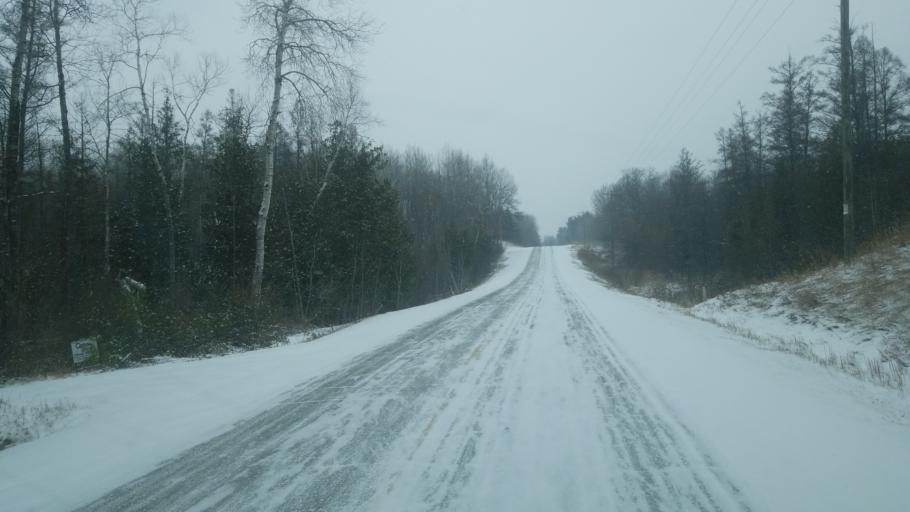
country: US
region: Michigan
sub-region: Osceola County
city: Reed City
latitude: 43.8018
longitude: -85.4024
